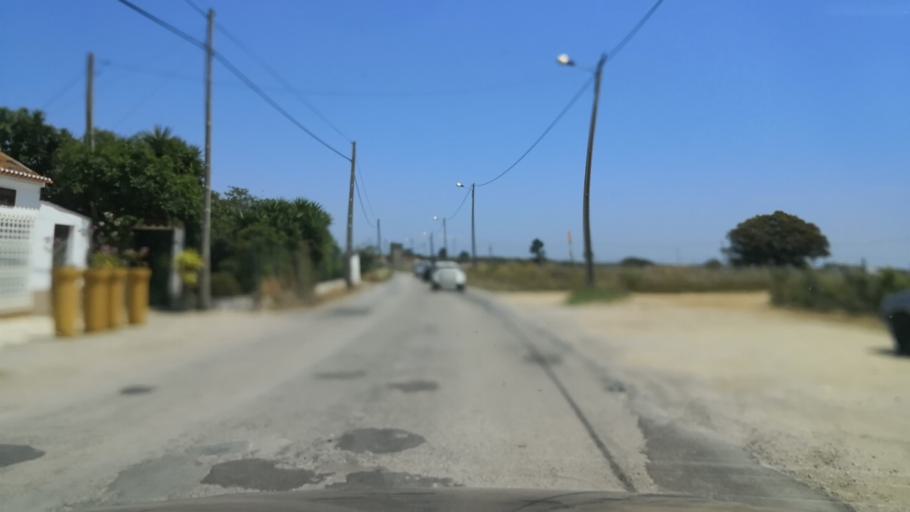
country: PT
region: Setubal
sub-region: Palmela
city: Palmela
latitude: 38.6007
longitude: -8.7962
